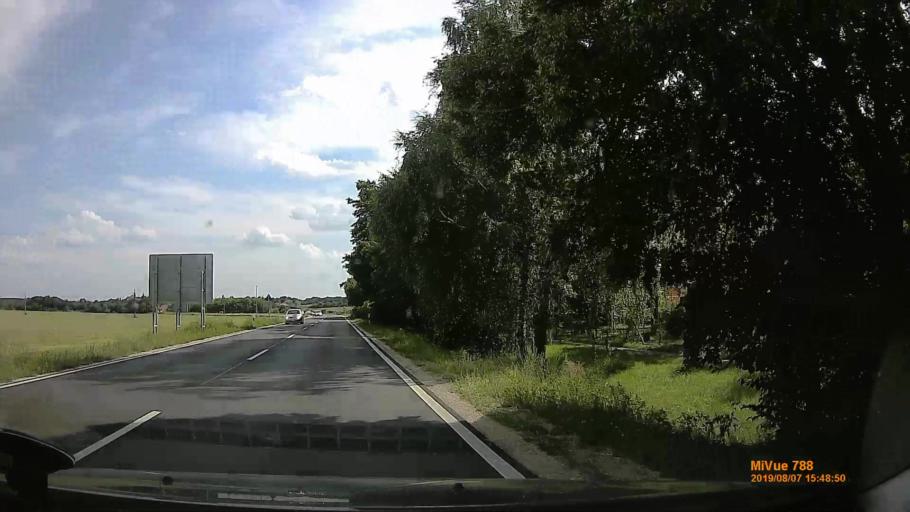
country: HU
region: Vas
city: Jak
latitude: 47.1572
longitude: 16.6383
